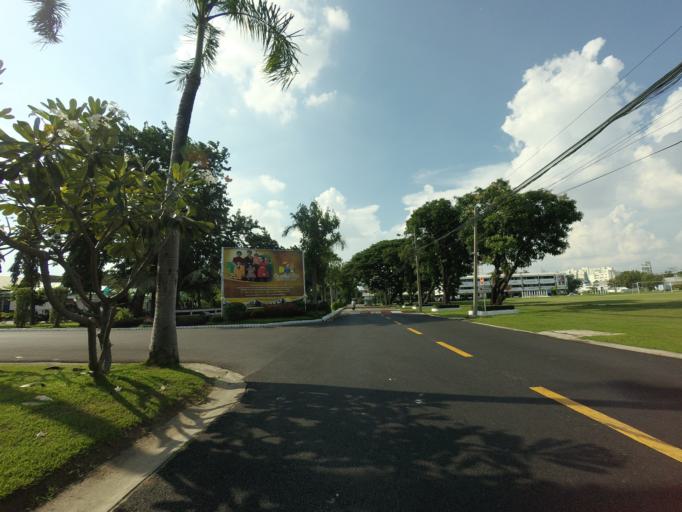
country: TH
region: Bangkok
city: Din Daeng
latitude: 13.7799
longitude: 100.5538
